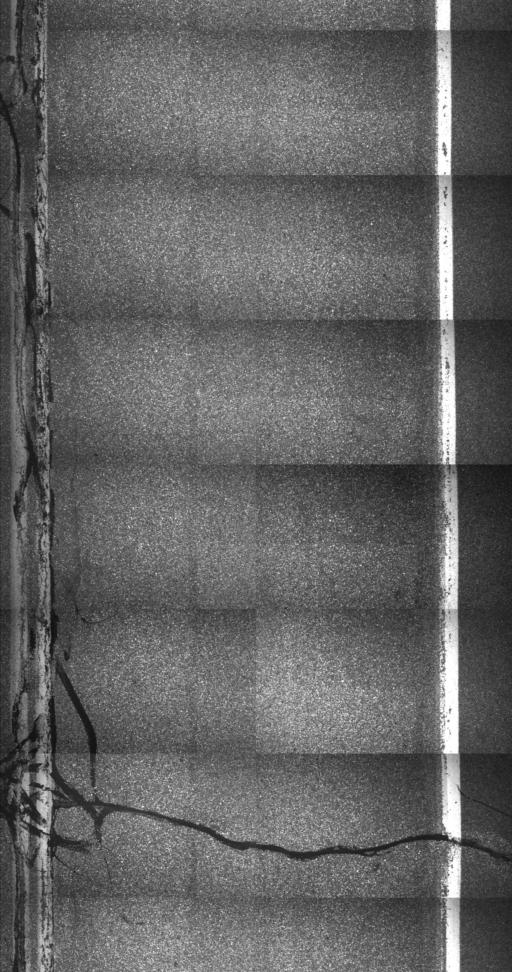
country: US
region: Vermont
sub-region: Lamoille County
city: Morrisville
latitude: 44.4609
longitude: -72.5451
